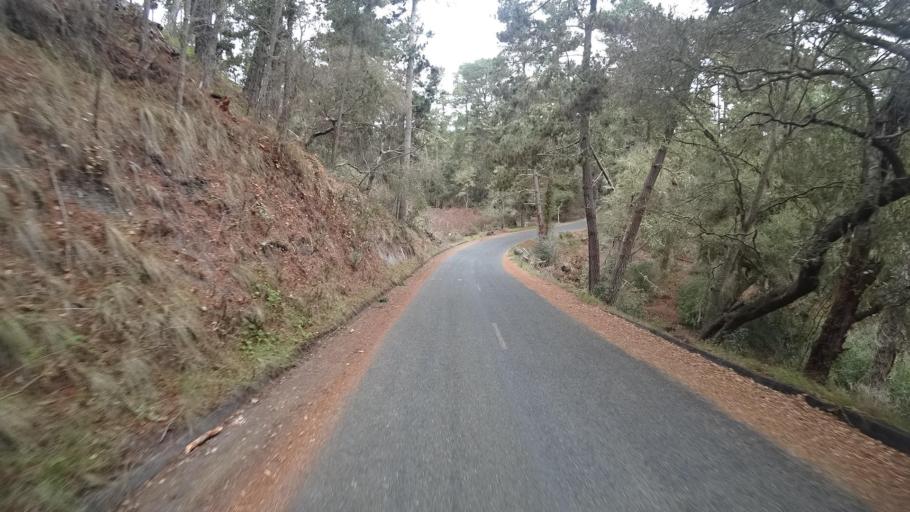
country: US
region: California
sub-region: Monterey County
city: Del Rey Oaks
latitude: 36.5635
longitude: -121.8602
